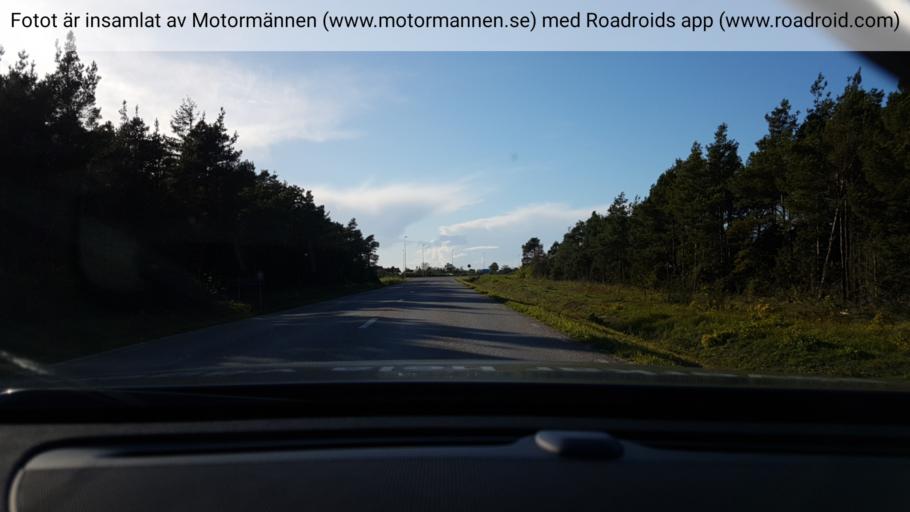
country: SE
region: Gotland
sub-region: Gotland
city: Klintehamn
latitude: 57.3801
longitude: 18.2036
